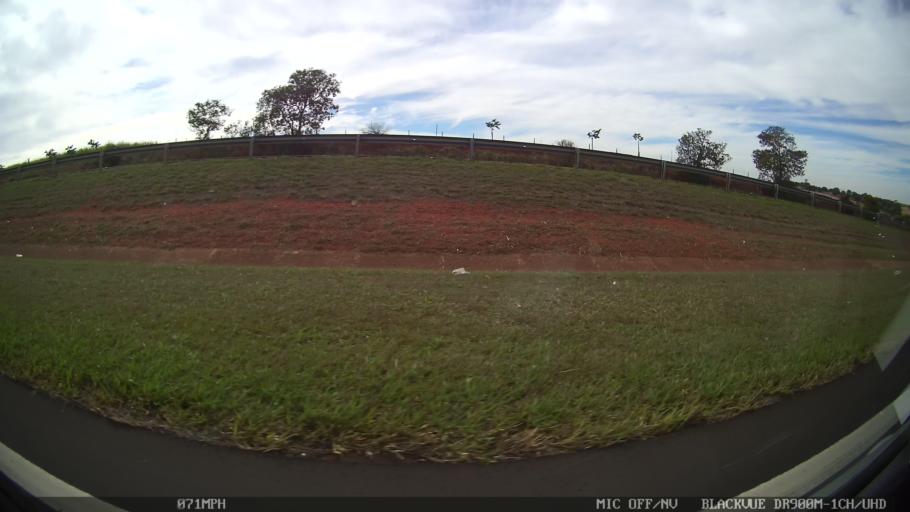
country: BR
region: Sao Paulo
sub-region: Taquaritinga
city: Taquaritinga
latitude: -21.5060
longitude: -48.5547
